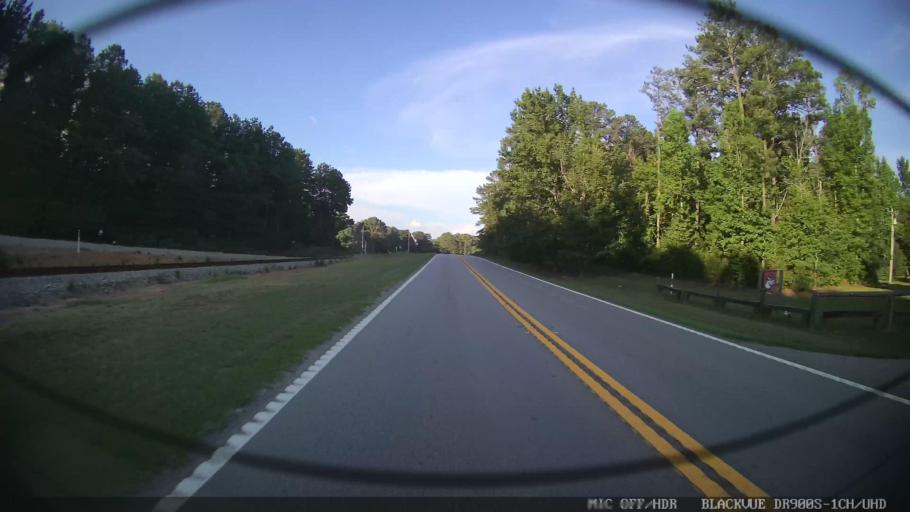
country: US
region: Georgia
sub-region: Monroe County
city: Forsyth
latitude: 32.9570
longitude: -83.8358
